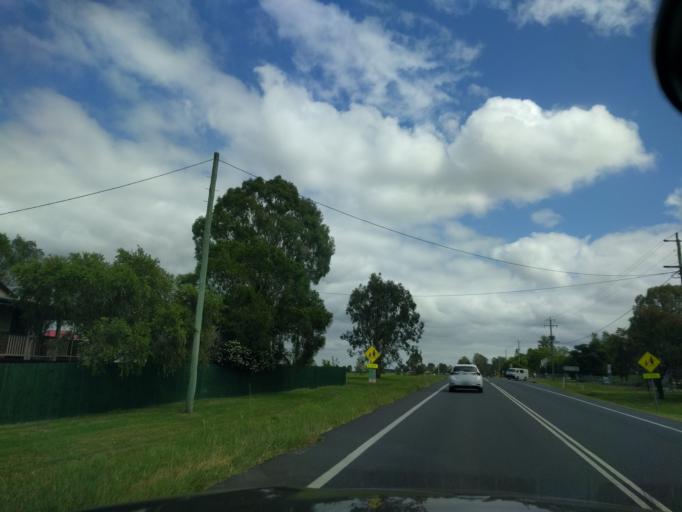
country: AU
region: Queensland
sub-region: Logan
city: Cedar Vale
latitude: -27.8948
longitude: 152.9739
